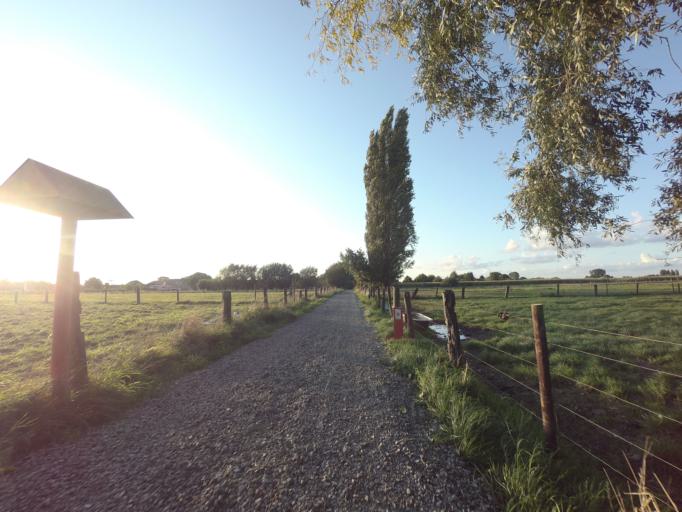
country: BE
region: Flanders
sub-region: Provincie Vlaams-Brabant
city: Londerzeel
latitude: 50.9908
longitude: 4.3296
